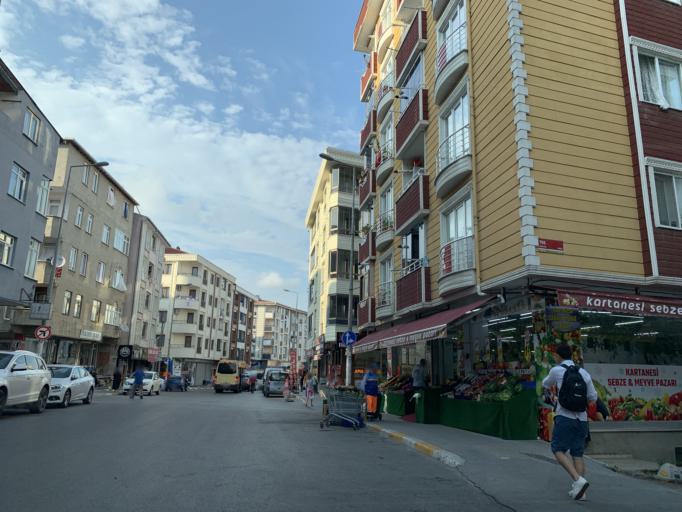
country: TR
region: Istanbul
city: Esenyurt
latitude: 41.0449
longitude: 28.6790
